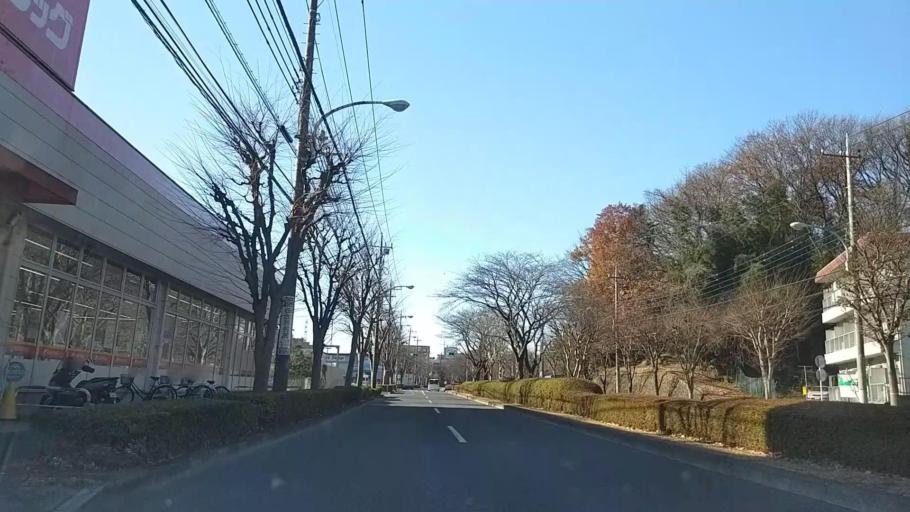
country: JP
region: Tokyo
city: Hino
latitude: 35.6413
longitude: 139.4266
